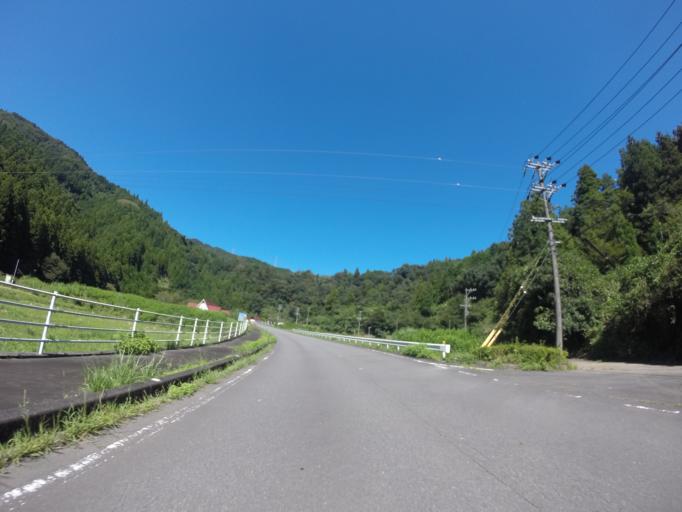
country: JP
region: Shizuoka
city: Kanaya
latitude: 34.9182
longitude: 138.1275
